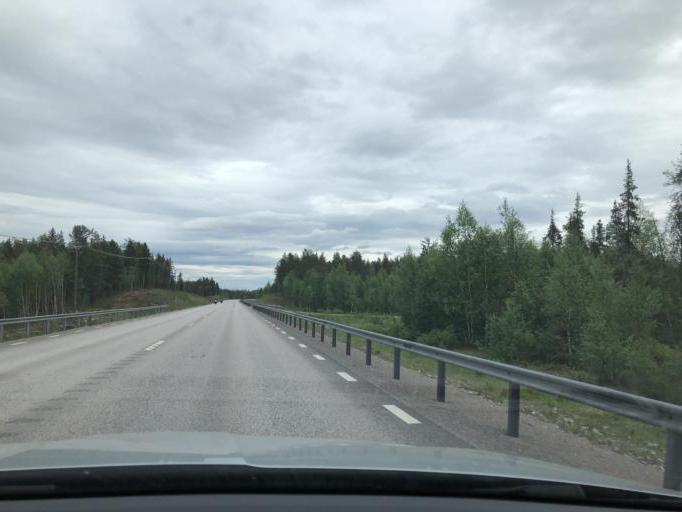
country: SE
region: Norrbotten
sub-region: Gallivare Kommun
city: Malmberget
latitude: 67.6422
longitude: 21.1012
